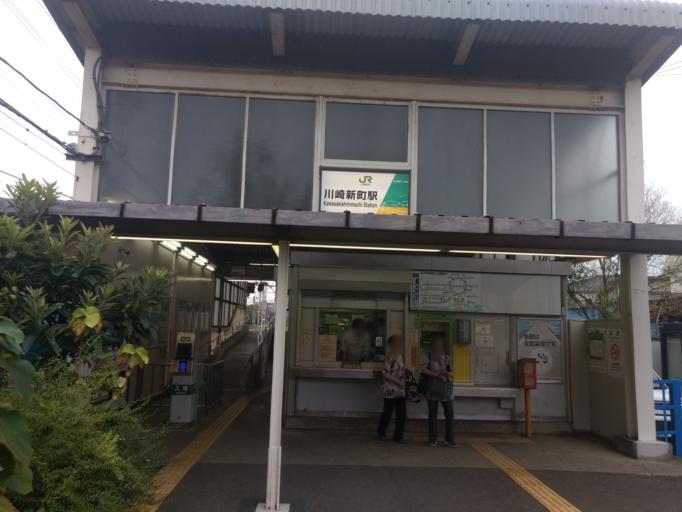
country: JP
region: Kanagawa
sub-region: Kawasaki-shi
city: Kawasaki
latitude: 35.5183
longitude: 139.6991
